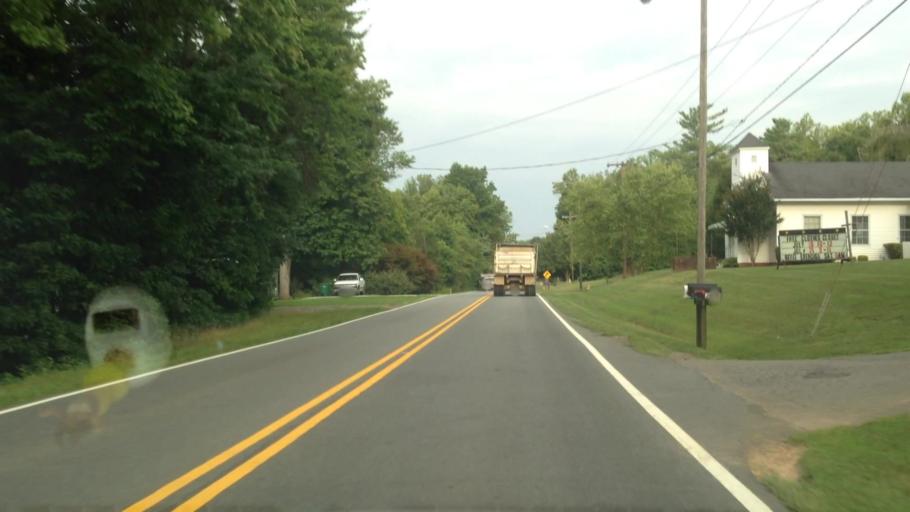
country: US
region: North Carolina
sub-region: Forsyth County
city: Walkertown
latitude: 36.1779
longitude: -80.1813
